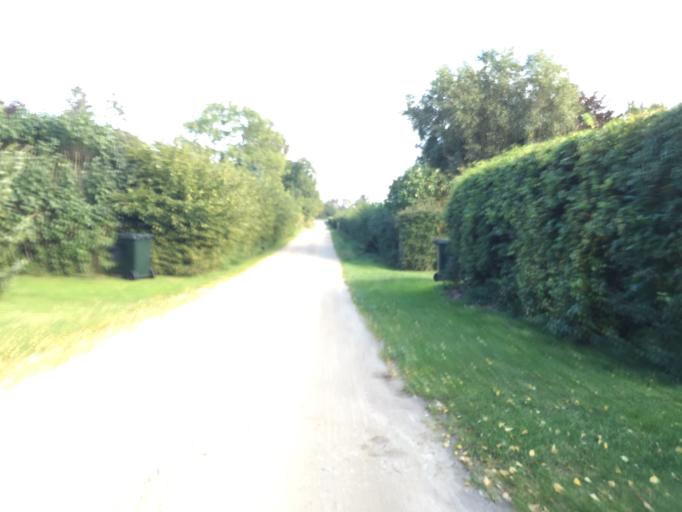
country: DK
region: Zealand
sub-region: Odsherred Kommune
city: Hojby
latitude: 55.8974
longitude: 11.5623
